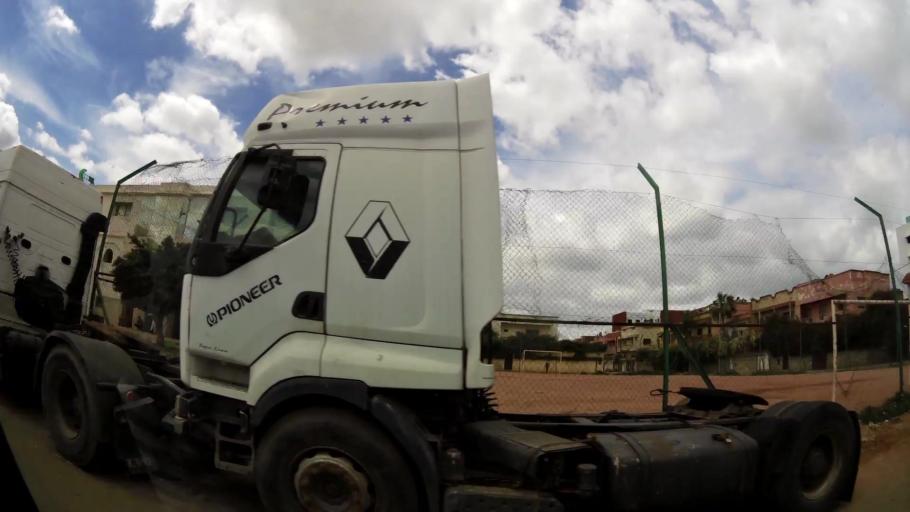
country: MA
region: Grand Casablanca
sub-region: Casablanca
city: Casablanca
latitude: 33.6139
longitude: -7.5461
